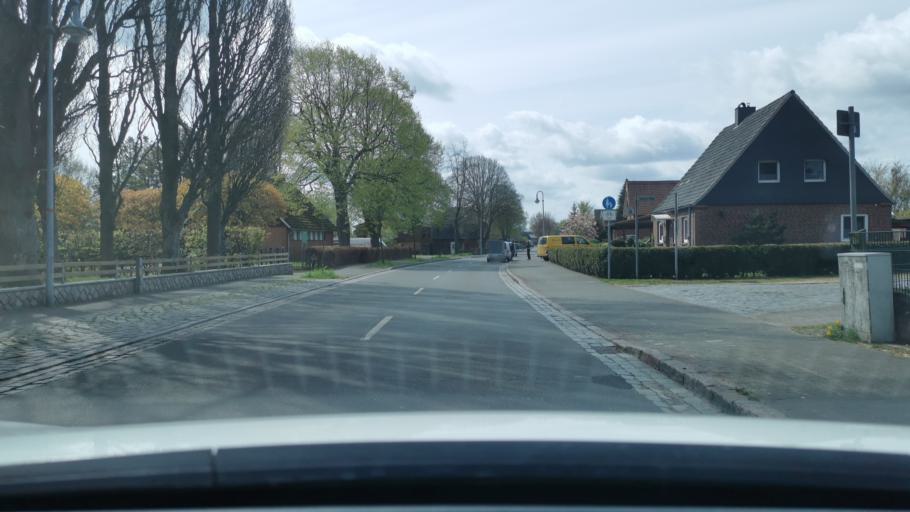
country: DE
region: Schleswig-Holstein
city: Hamdorf
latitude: 54.2225
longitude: 9.5189
